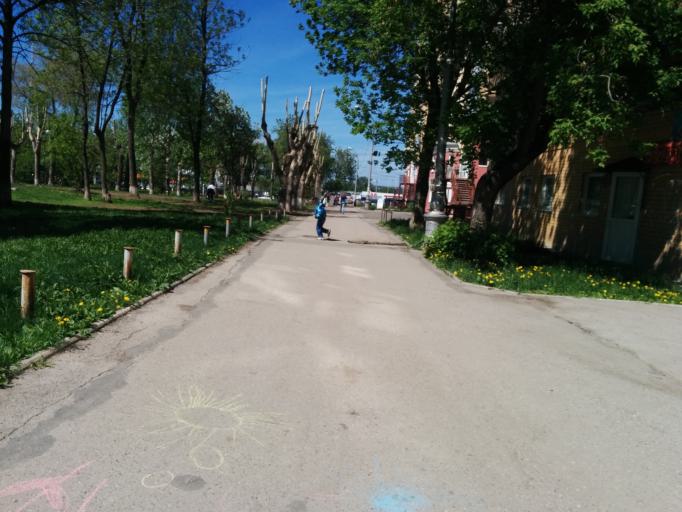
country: RU
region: Perm
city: Perm
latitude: 58.0216
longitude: 56.2873
